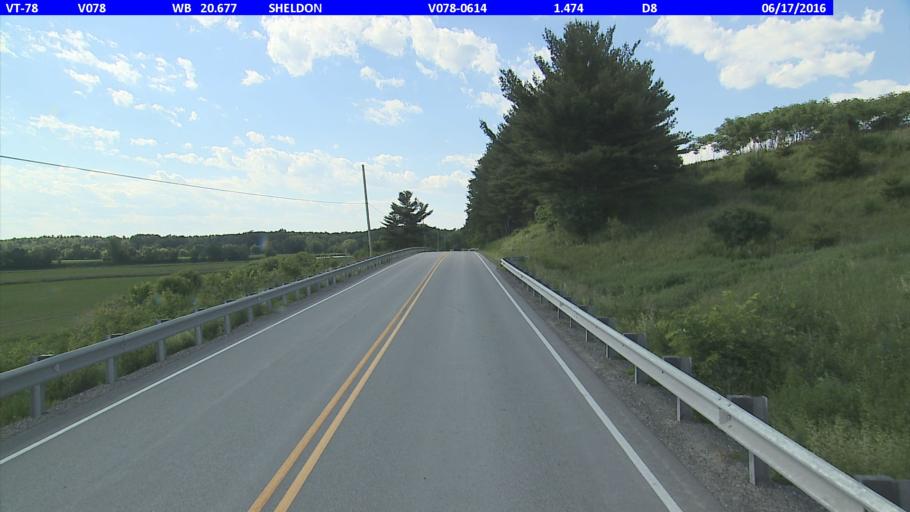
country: US
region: Vermont
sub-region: Franklin County
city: Enosburg Falls
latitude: 44.9073
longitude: -72.9514
